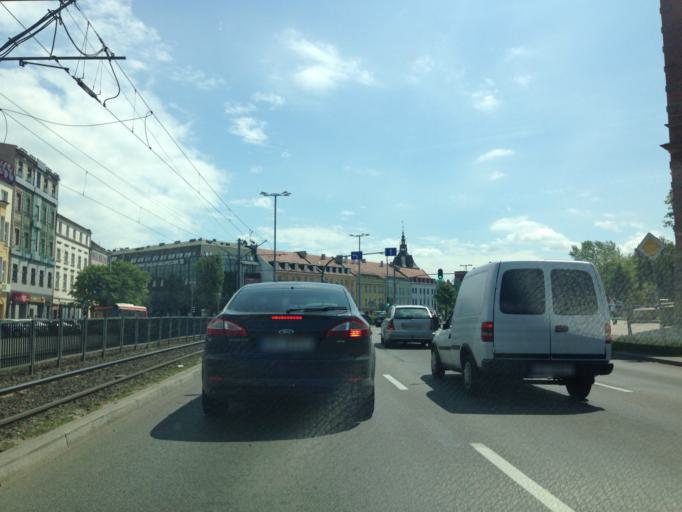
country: PL
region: Pomeranian Voivodeship
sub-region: Gdansk
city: Gdansk
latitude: 54.3529
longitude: 18.6456
